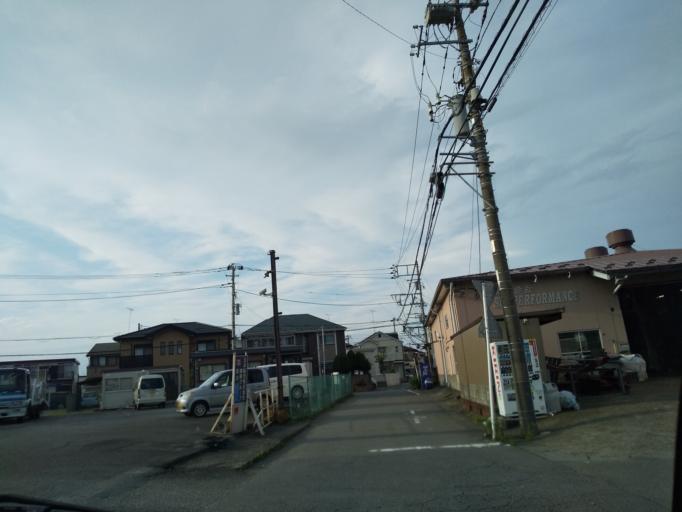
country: JP
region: Kanagawa
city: Zama
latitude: 35.5104
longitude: 139.3617
